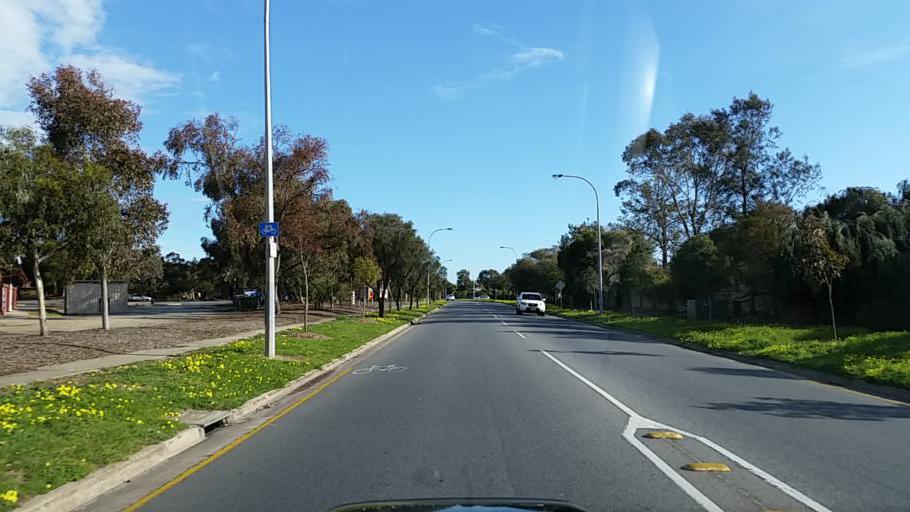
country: AU
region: South Australia
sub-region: Charles Sturt
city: West Lakes Shore
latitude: -34.8651
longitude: 138.4853
